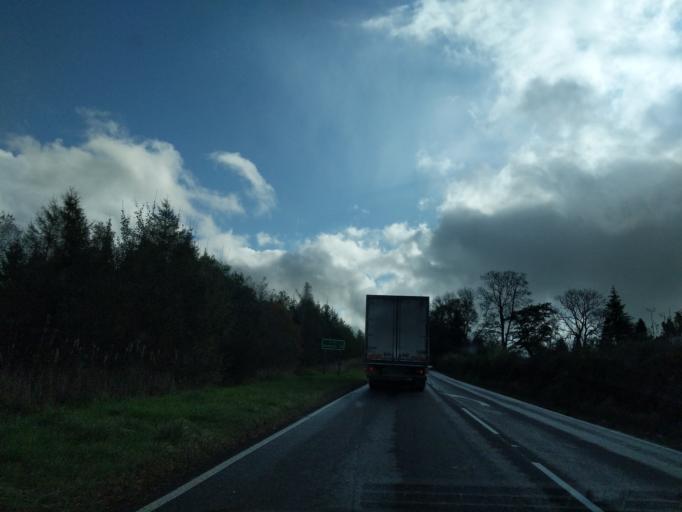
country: GB
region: Scotland
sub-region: Dumfries and Galloway
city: Moffat
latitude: 55.2835
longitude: -3.4440
